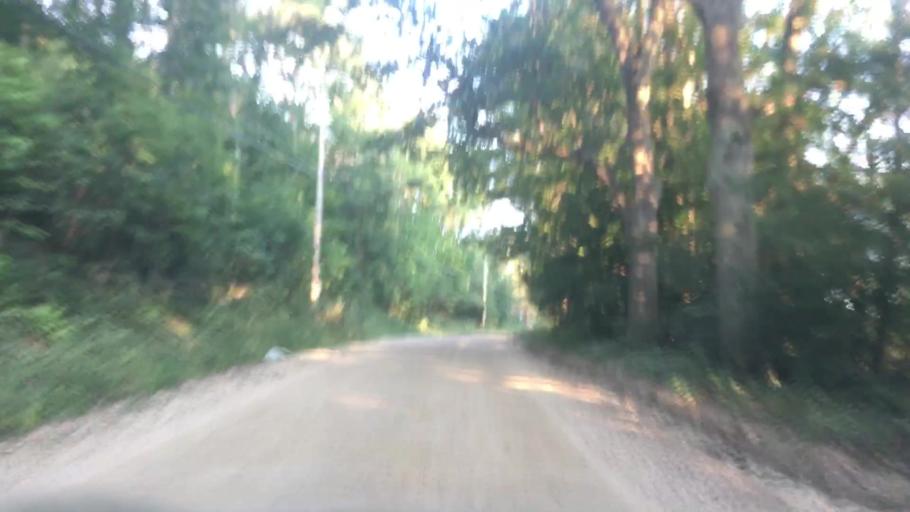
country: US
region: New Hampshire
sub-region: Belknap County
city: Barnstead
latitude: 43.4084
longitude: -71.2717
